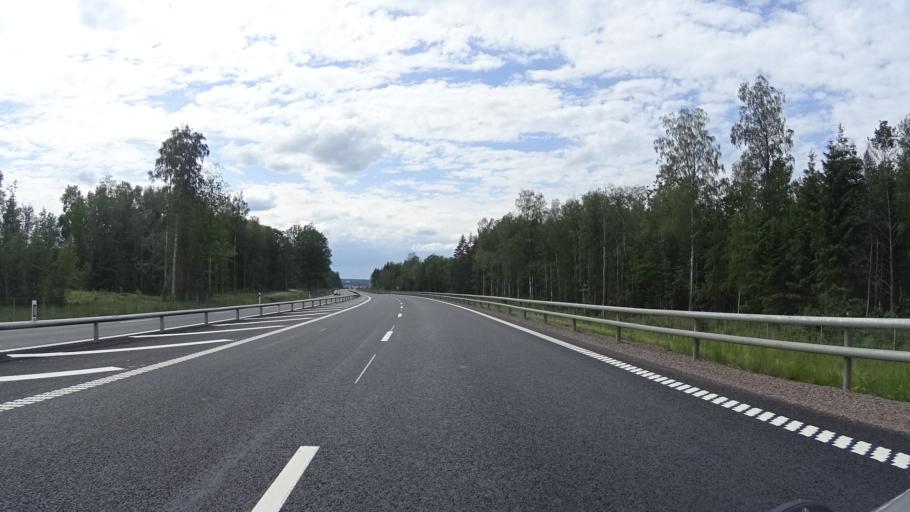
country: SE
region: Vaestra Goetaland
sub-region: Gullspangs Kommun
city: Anderstorp
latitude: 58.8798
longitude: 14.2718
